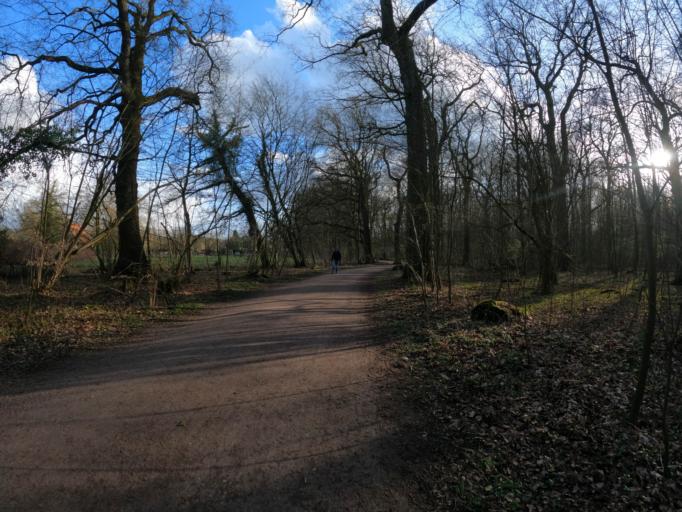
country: DE
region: Hamburg
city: Stellingen
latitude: 53.6105
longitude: 9.9389
